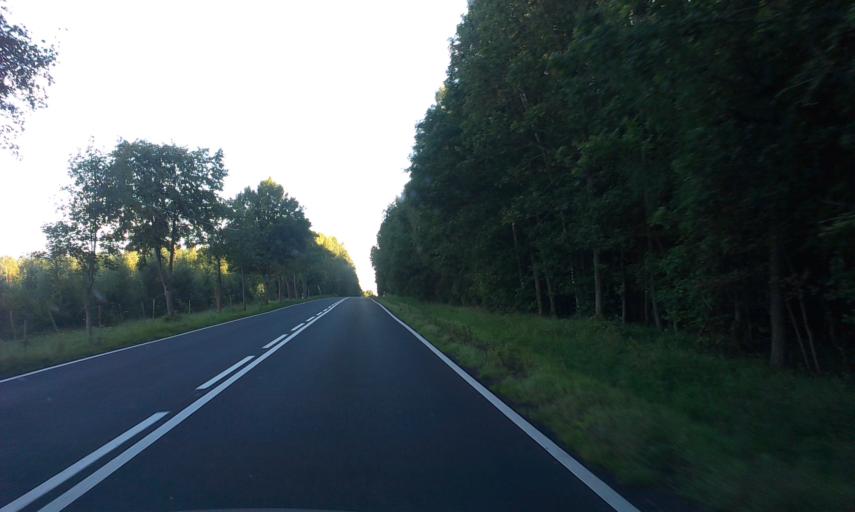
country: PL
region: West Pomeranian Voivodeship
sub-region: Powiat szczecinecki
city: Szczecinek
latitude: 53.8248
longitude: 16.6389
